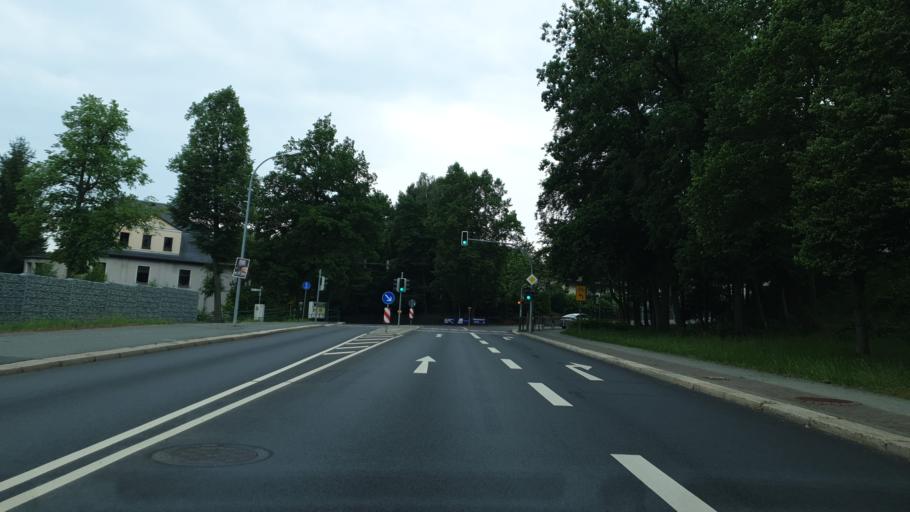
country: DE
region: Saxony
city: Auerbach
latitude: 50.5245
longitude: 12.3994
